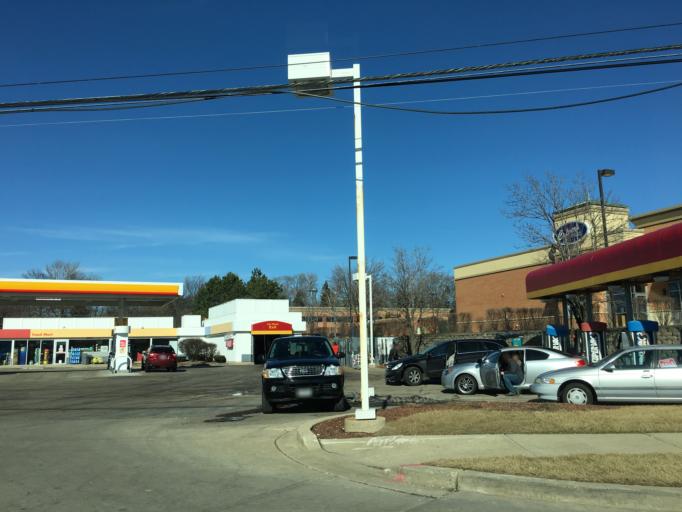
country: US
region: Illinois
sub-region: Cook County
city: Rolling Meadows
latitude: 42.0683
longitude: -88.0432
